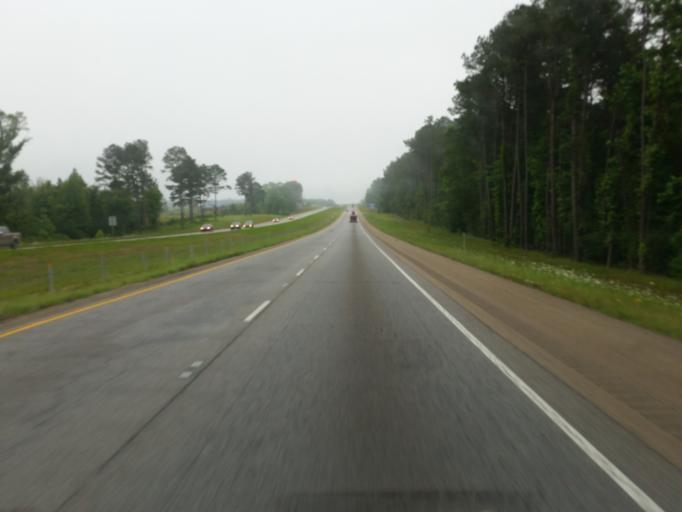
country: US
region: Louisiana
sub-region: Webster Parish
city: Minden
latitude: 32.5831
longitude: -93.2611
